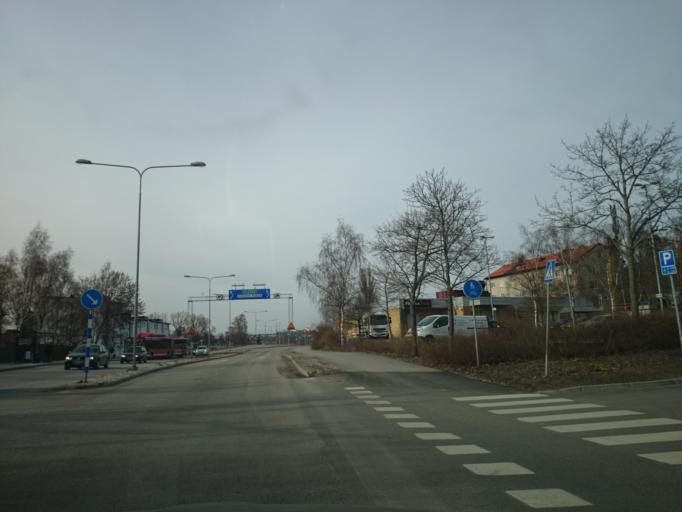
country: SE
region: Stockholm
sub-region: Huddinge Kommun
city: Segeltorp
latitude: 59.2786
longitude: 17.9435
